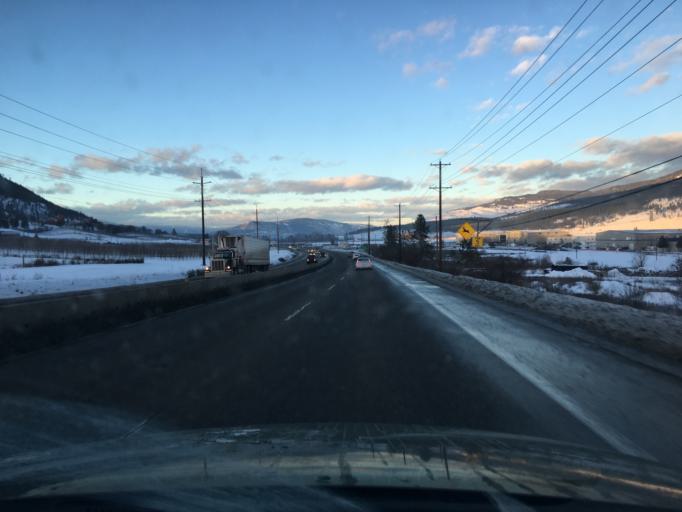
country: CA
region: British Columbia
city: Kelowna
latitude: 49.9646
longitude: -119.3844
